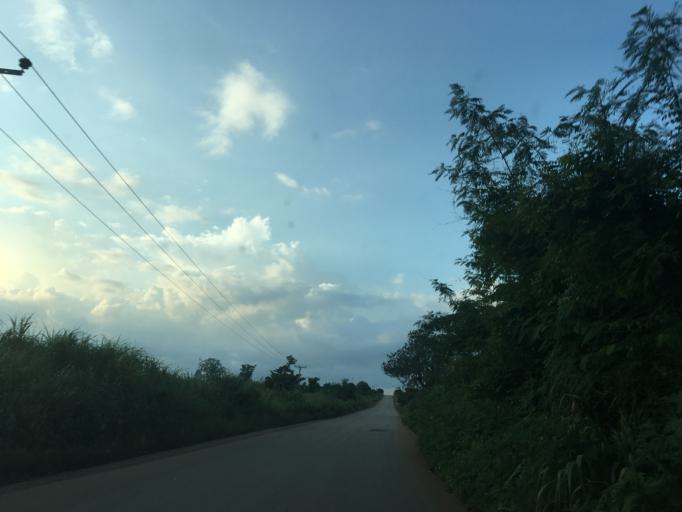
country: GH
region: Western
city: Bibiani
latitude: 6.6377
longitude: -2.4252
